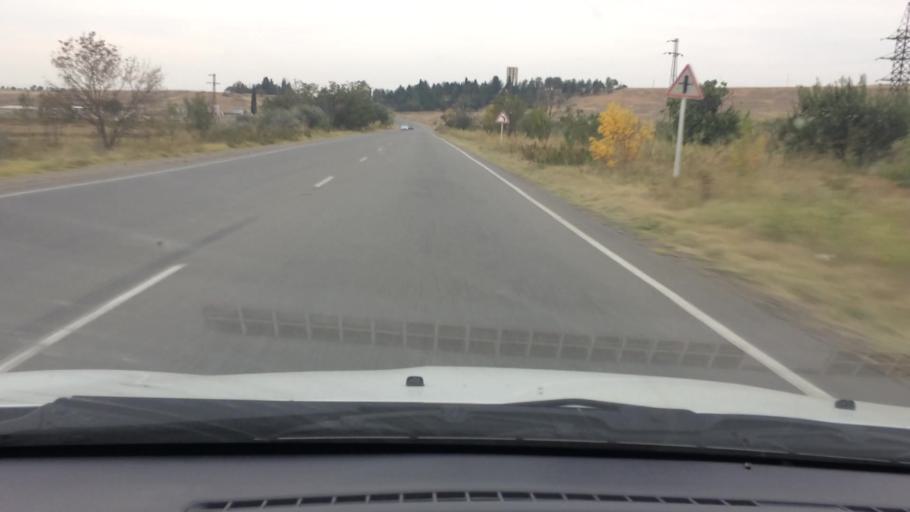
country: GE
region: Kvemo Kartli
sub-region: Marneuli
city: Marneuli
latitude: 41.5297
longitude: 44.7770
